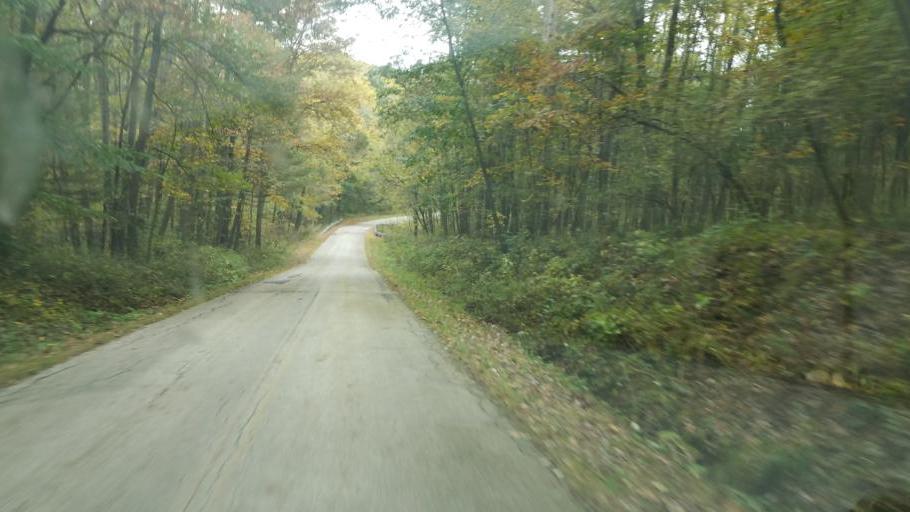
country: US
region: Ohio
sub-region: Ashland County
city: Loudonville
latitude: 40.5608
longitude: -82.1542
